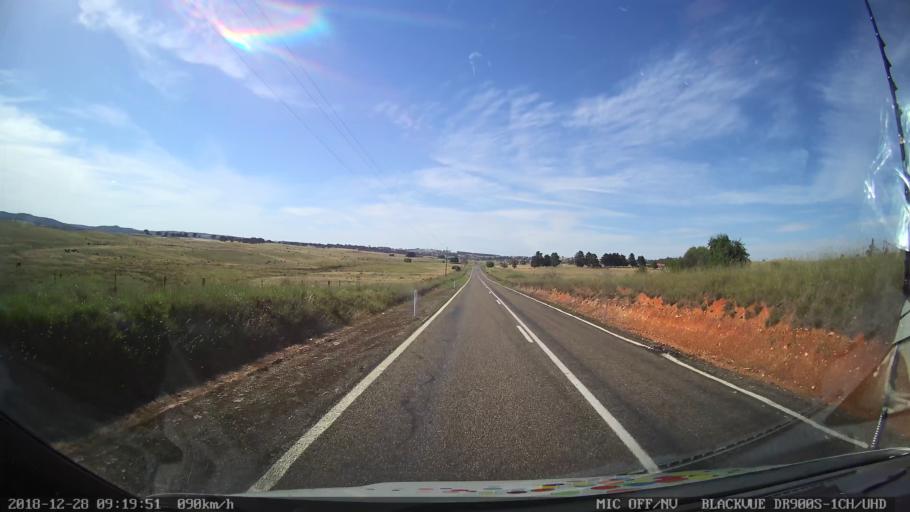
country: AU
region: New South Wales
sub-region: Upper Lachlan Shire
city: Crookwell
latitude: -34.3423
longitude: 149.3706
